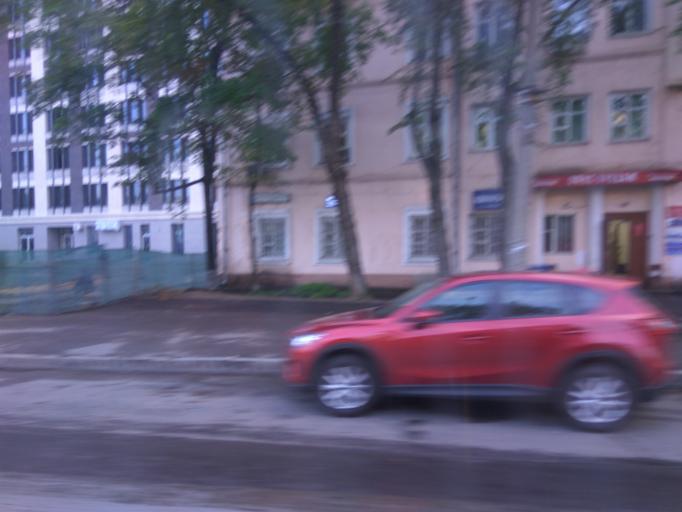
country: RU
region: Moskovskaya
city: Bogorodskoye
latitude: 55.8003
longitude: 37.7124
